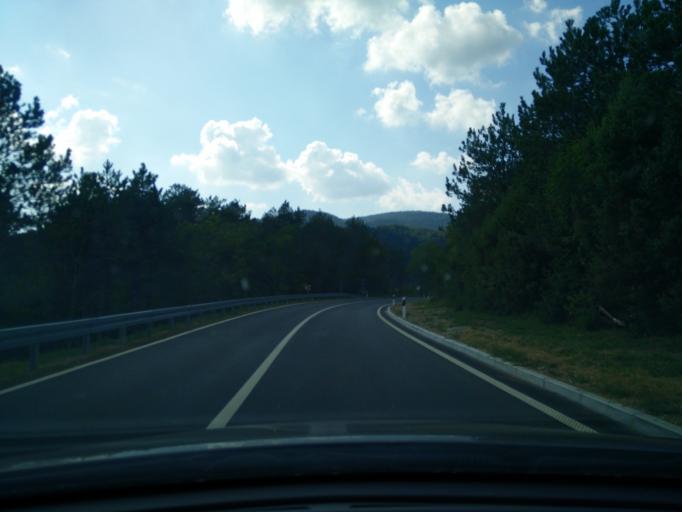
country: HR
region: Istarska
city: Buzet
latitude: 45.4366
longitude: 13.9362
